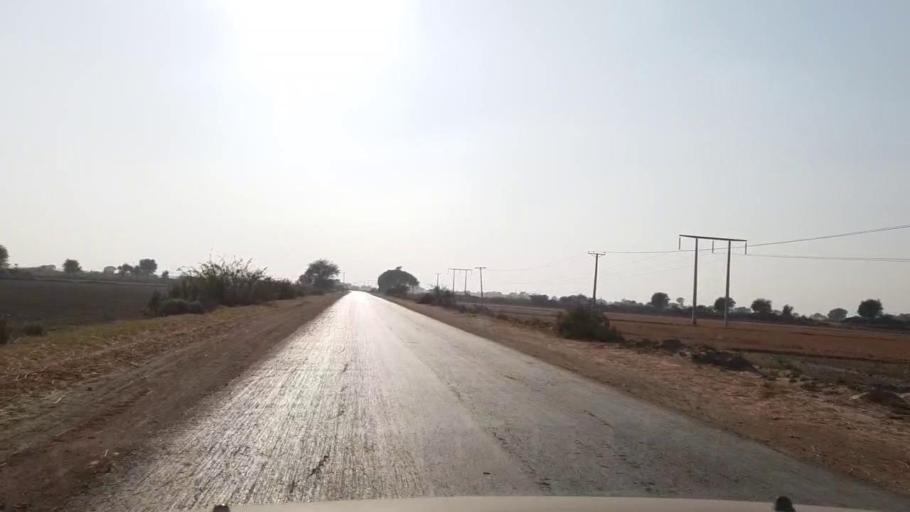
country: PK
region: Sindh
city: Bulri
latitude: 24.9909
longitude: 68.3787
